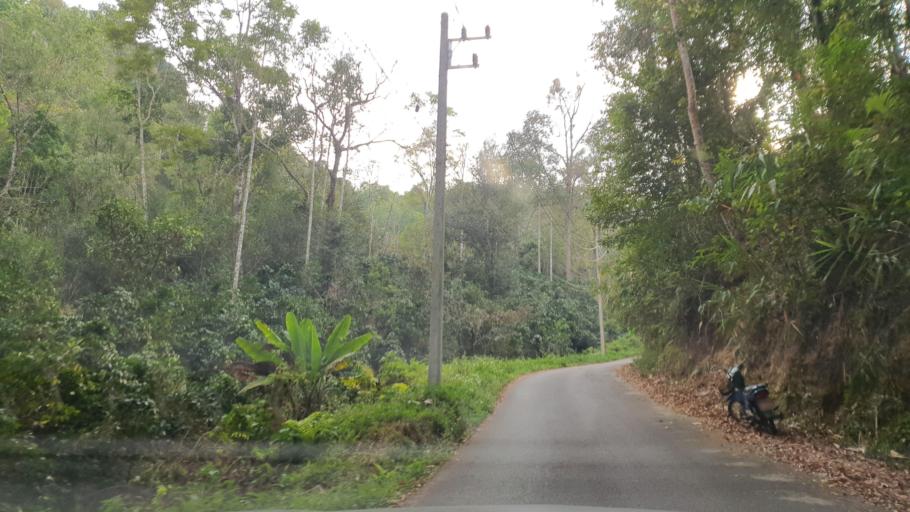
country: TH
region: Chiang Mai
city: Mae On
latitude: 18.9440
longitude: 99.3592
